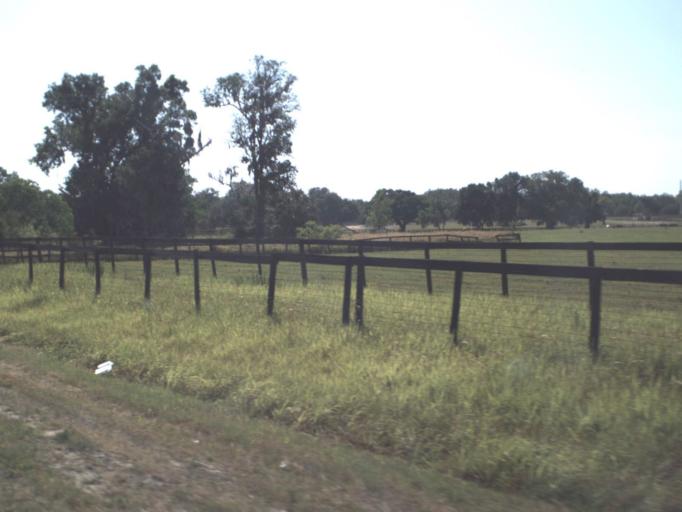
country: US
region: Florida
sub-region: Marion County
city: Dunnellon
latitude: 29.1623
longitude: -82.3446
